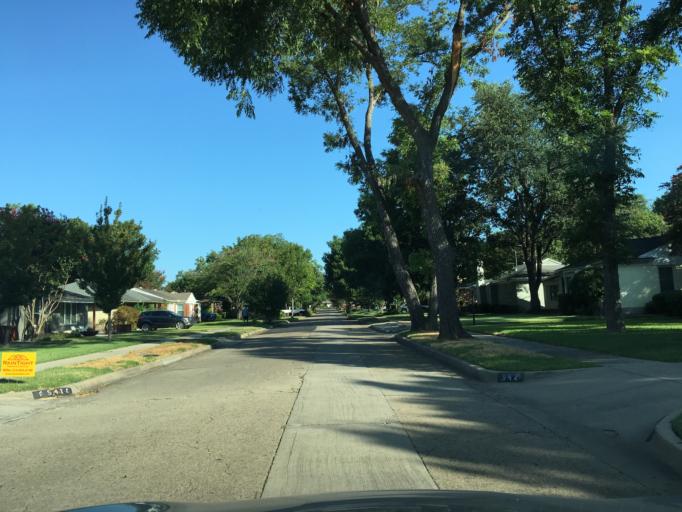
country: US
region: Texas
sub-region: Dallas County
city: Highland Park
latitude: 32.8550
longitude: -96.7072
